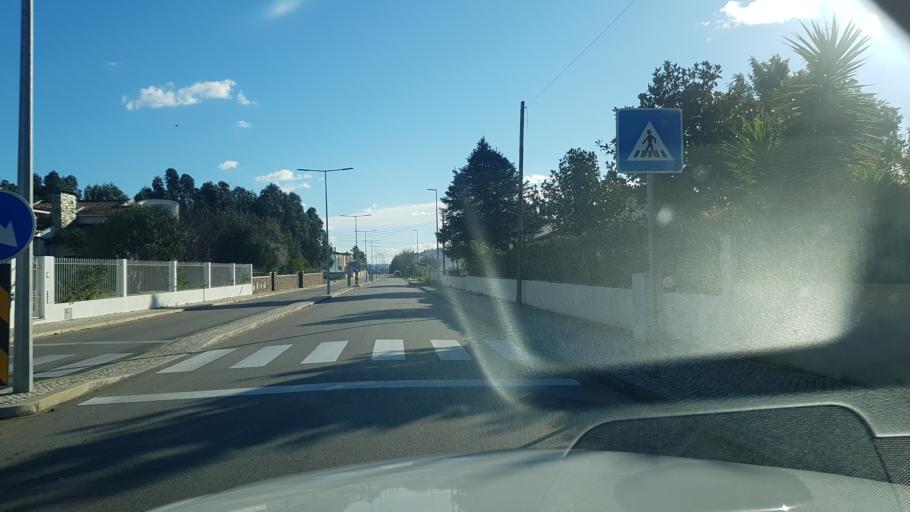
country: PT
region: Santarem
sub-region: Entroncamento
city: Entroncamento
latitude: 39.4807
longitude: -8.4685
